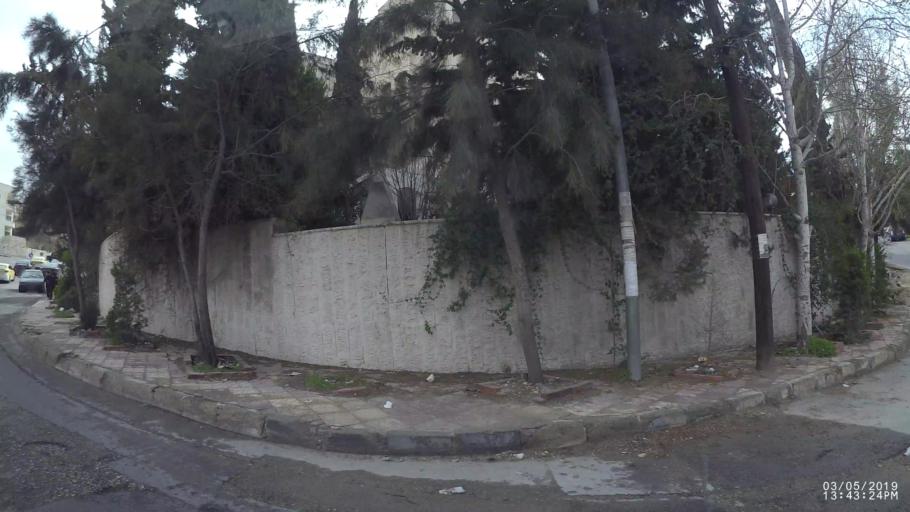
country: JO
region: Amman
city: Amman
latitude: 32.0059
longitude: 35.9394
